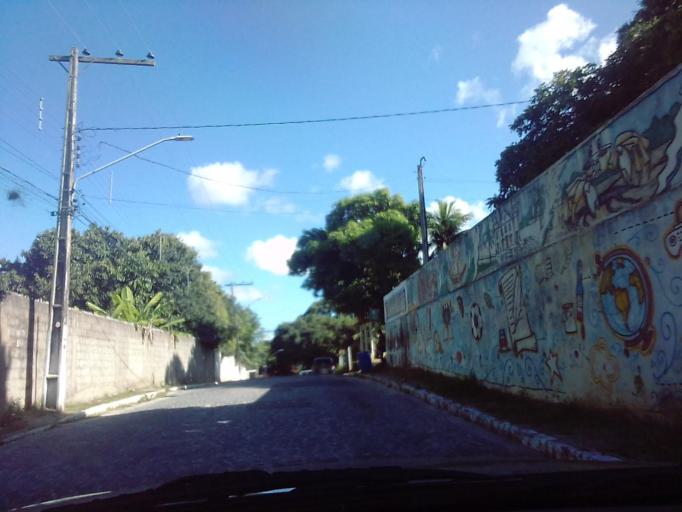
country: BR
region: Pernambuco
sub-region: Igarassu
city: Igarassu
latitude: -7.8473
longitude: -34.8428
